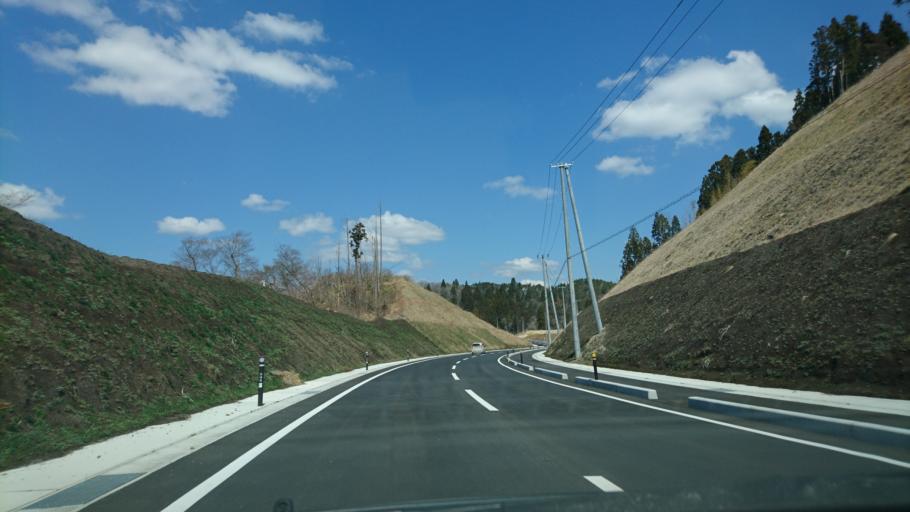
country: JP
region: Iwate
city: Ofunato
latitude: 38.8909
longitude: 141.5990
